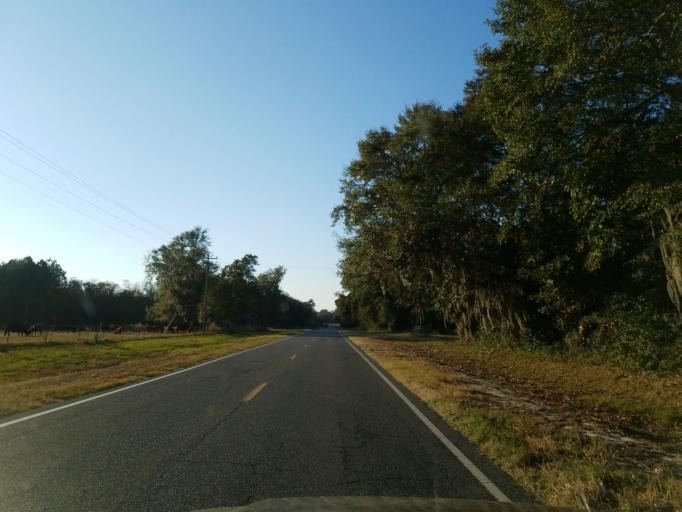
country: US
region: Georgia
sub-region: Berrien County
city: Nashville
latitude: 31.1896
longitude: -83.2023
